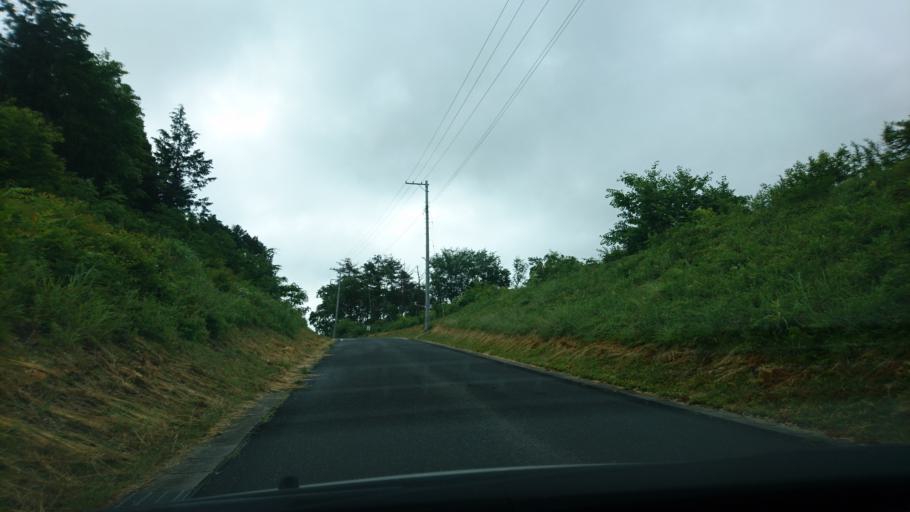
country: JP
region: Iwate
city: Ichinoseki
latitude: 38.9030
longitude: 141.1414
